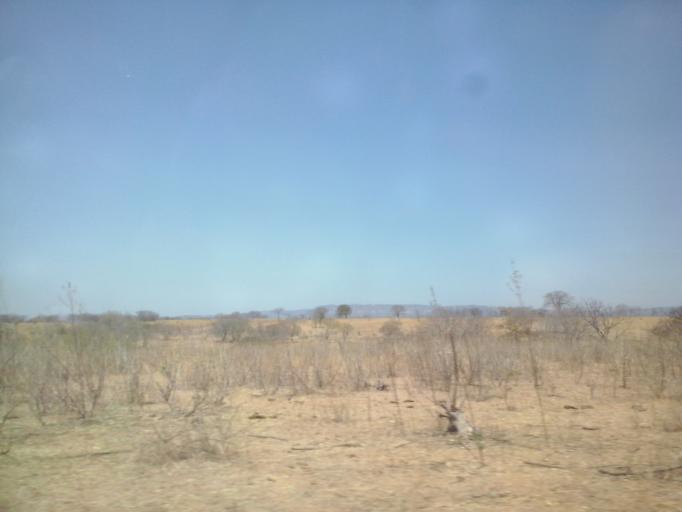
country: BR
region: Paraiba
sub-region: Paulista
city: Paulista
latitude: -6.5978
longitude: -37.6581
